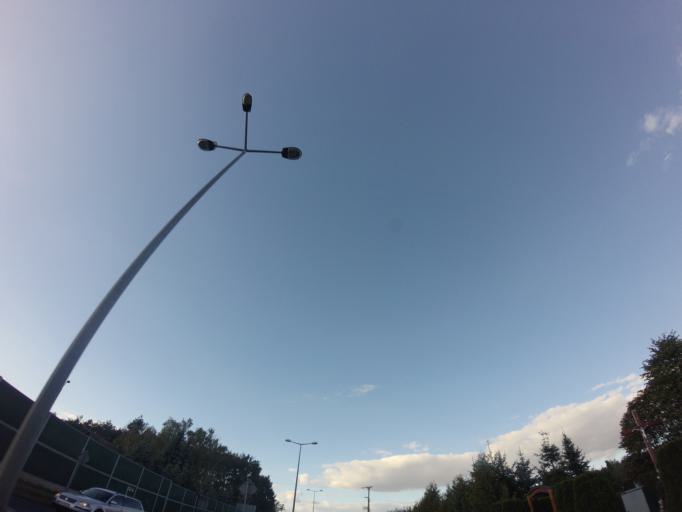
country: PL
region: Greater Poland Voivodeship
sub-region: Powiat nowotomyski
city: Nowy Tomysl
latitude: 52.3130
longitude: 16.1104
